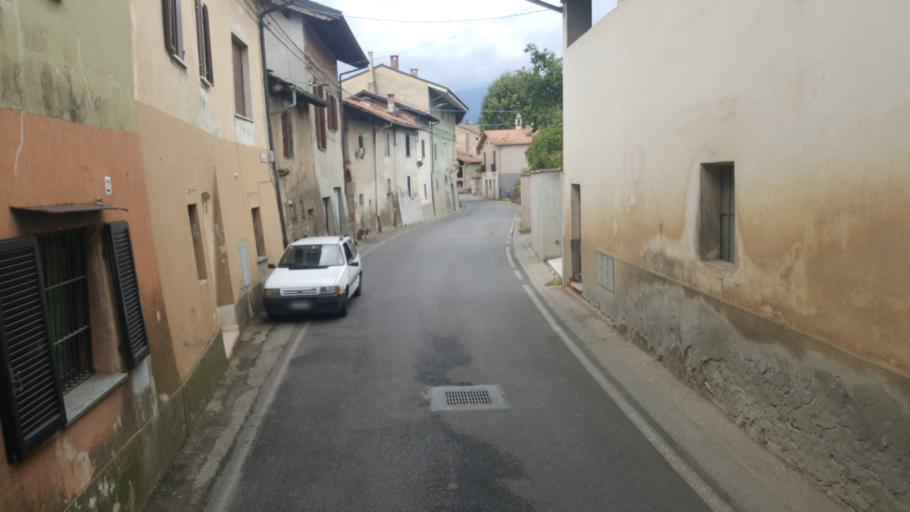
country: IT
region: Piedmont
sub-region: Provincia di Torino
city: San Ponso
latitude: 45.3506
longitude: 7.6704
